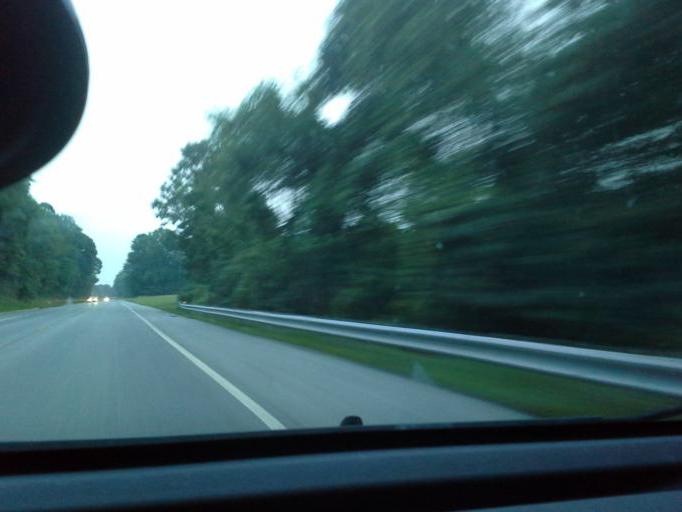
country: US
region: Maryland
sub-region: Calvert County
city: Owings
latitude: 38.7104
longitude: -76.5927
